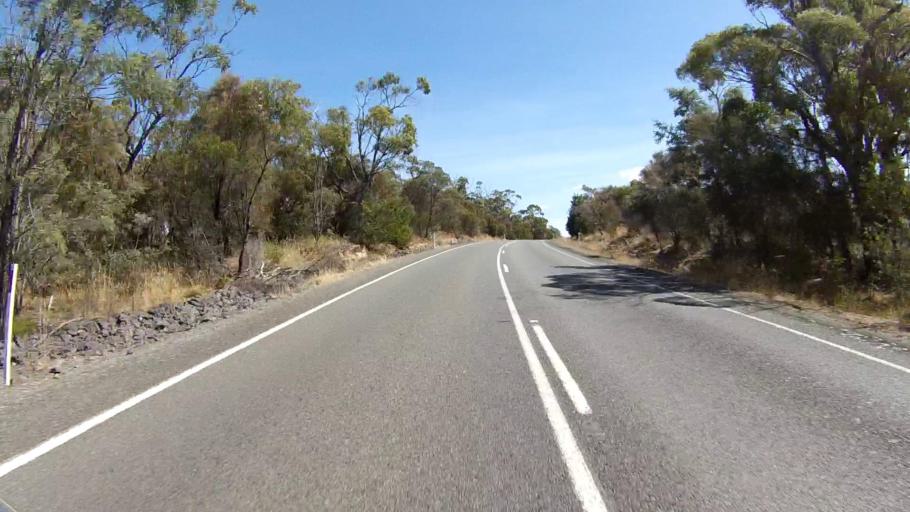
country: AU
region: Tasmania
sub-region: Sorell
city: Sorell
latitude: -42.5846
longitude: 147.8064
